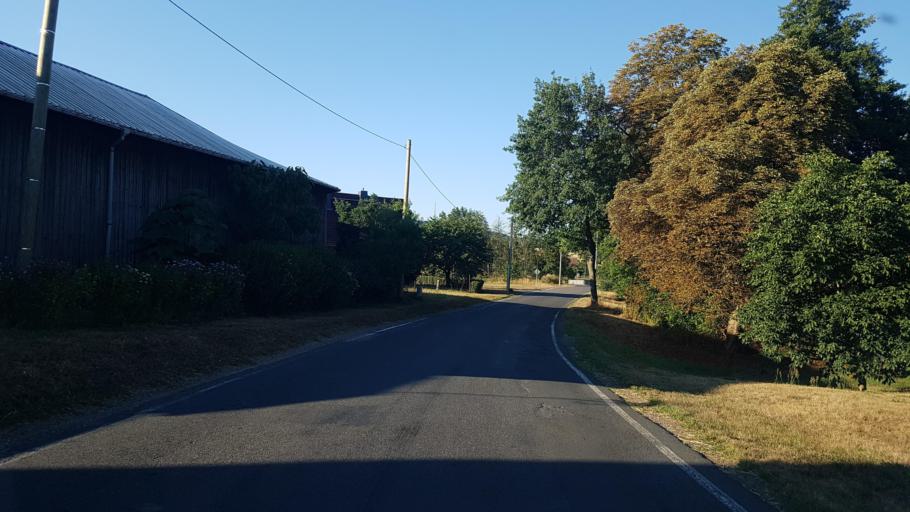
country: DE
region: Saxony
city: Dahlen
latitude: 51.3302
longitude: 13.0167
